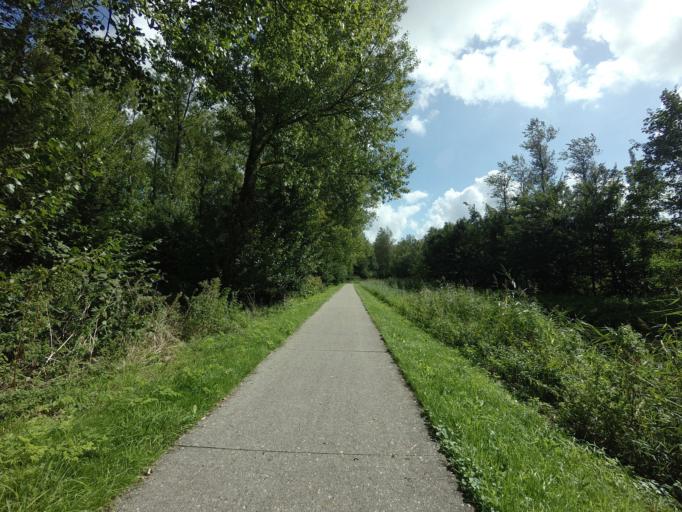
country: NL
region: North Holland
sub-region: Gemeente Purmerend
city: Purmerend
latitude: 52.4745
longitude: 4.9721
